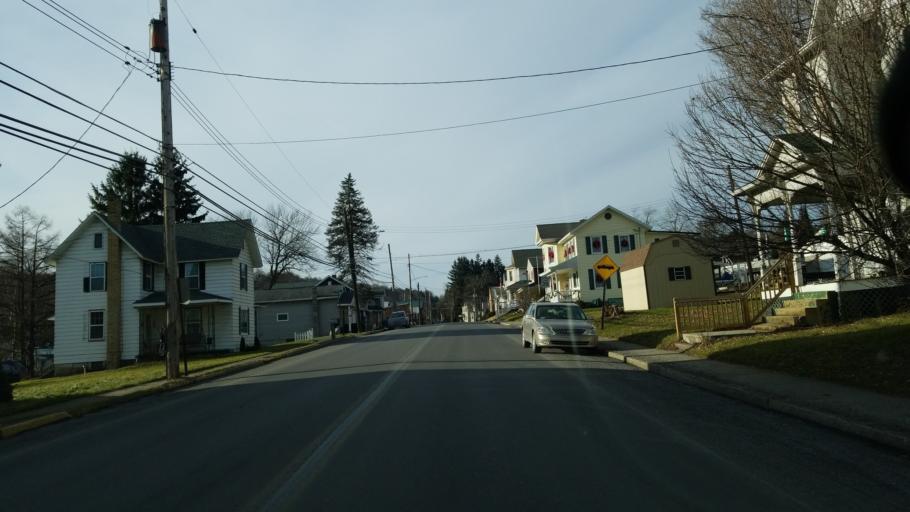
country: US
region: Pennsylvania
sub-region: Clearfield County
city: Curwensville
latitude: 40.9645
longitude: -78.6104
